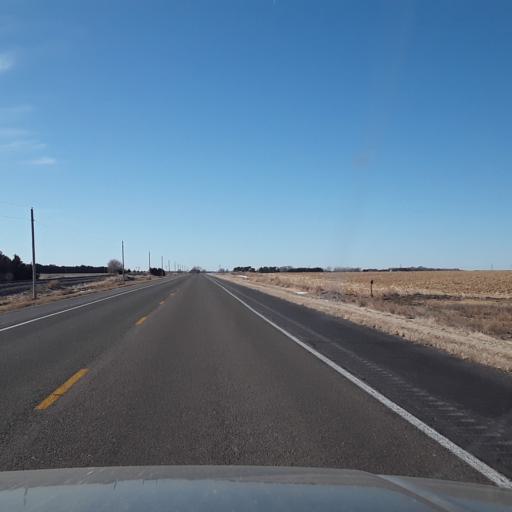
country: US
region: Nebraska
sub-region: Kearney County
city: Minden
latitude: 40.5443
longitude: -98.8465
